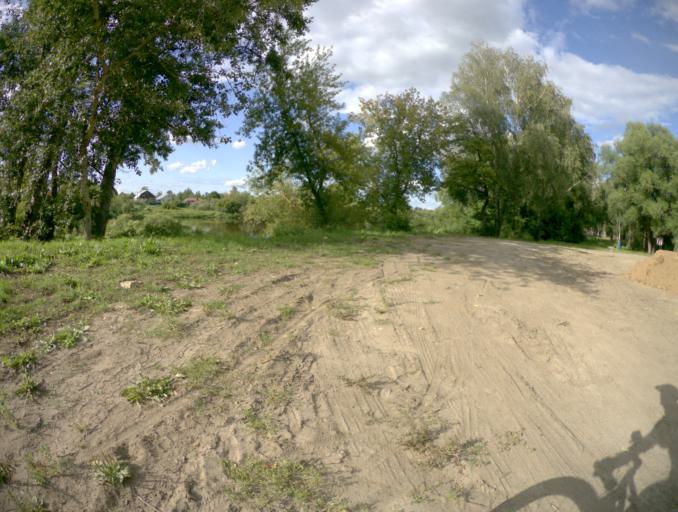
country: RU
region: Vladimir
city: Sobinka
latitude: 55.9961
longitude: 40.0179
